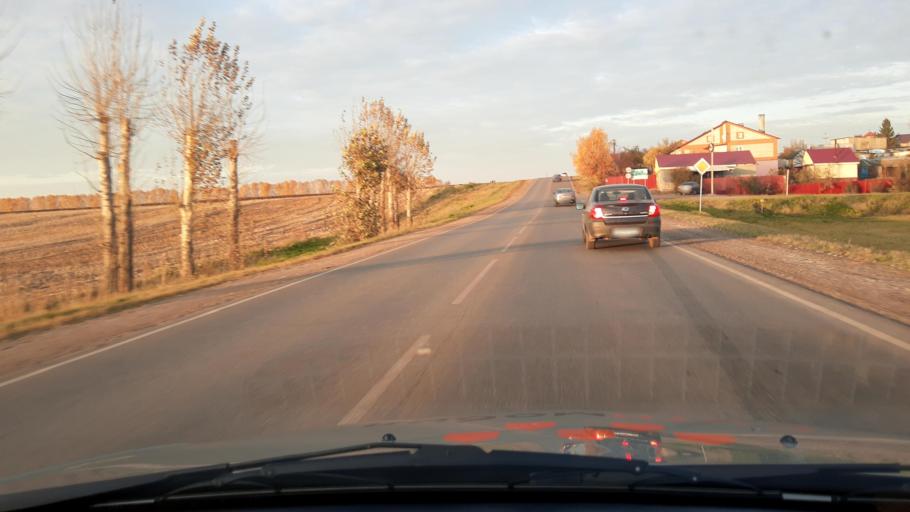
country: RU
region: Bashkortostan
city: Ufa
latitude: 54.8190
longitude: 55.9845
